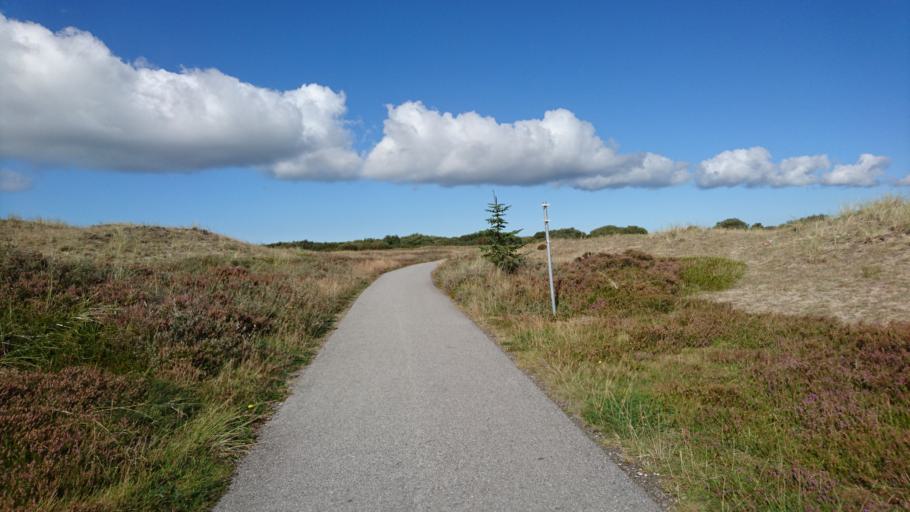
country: DK
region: North Denmark
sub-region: Frederikshavn Kommune
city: Skagen
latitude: 57.6738
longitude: 10.4979
